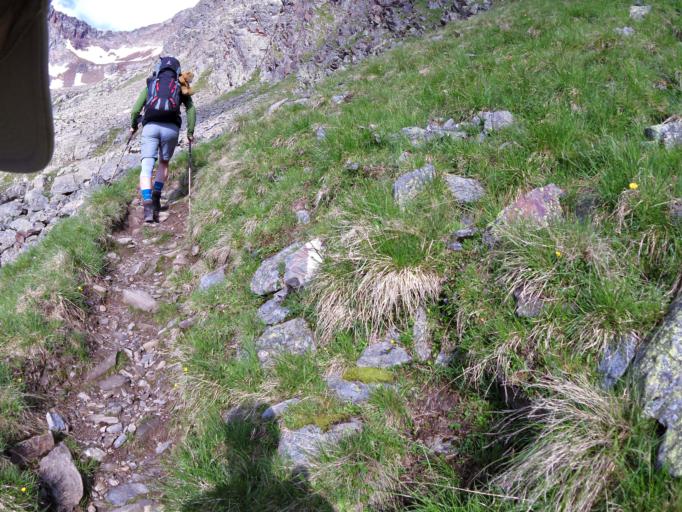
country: AT
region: Tyrol
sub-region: Politischer Bezirk Innsbruck Land
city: Gschnitz
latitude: 47.0420
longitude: 11.3075
